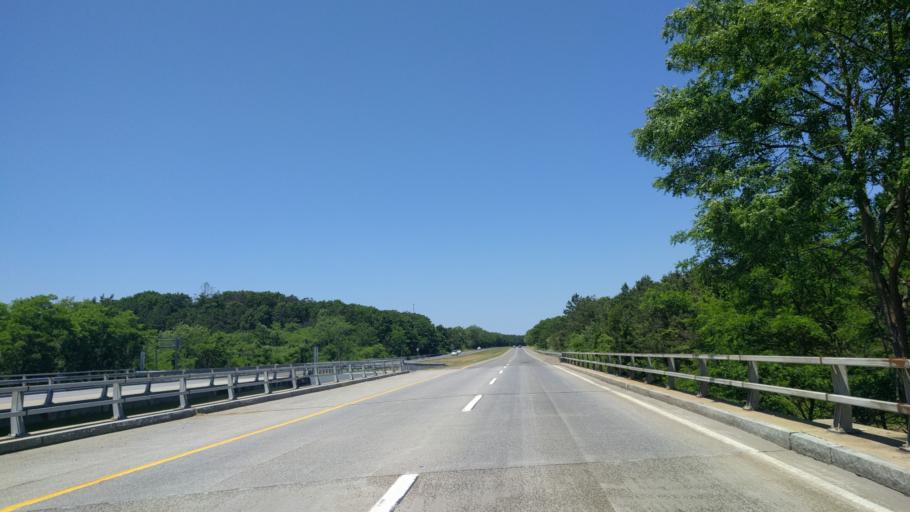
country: US
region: New York
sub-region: Suffolk County
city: Eastport
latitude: 40.8484
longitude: -72.7396
